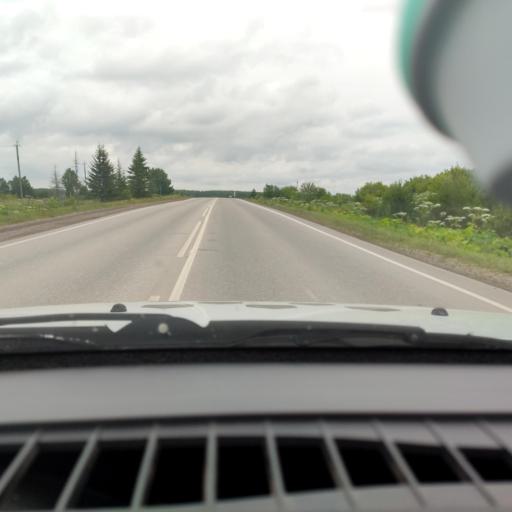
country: RU
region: Perm
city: Kungur
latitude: 57.4498
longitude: 57.0024
